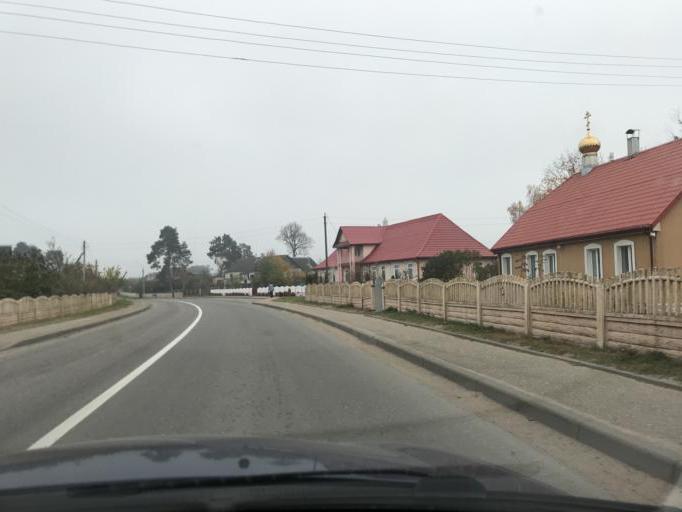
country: BY
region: Grodnenskaya
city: Hrodna
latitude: 53.8157
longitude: 23.8619
